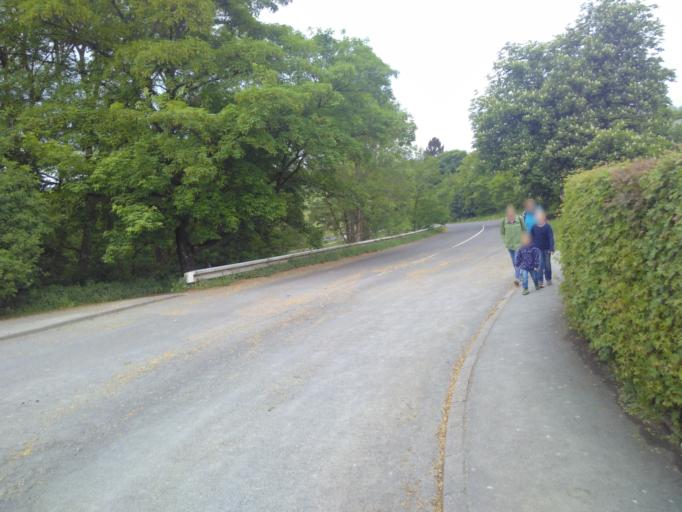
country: DE
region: Hesse
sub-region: Regierungsbezirk Kassel
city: Baunatal
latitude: 51.3165
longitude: 9.3917
